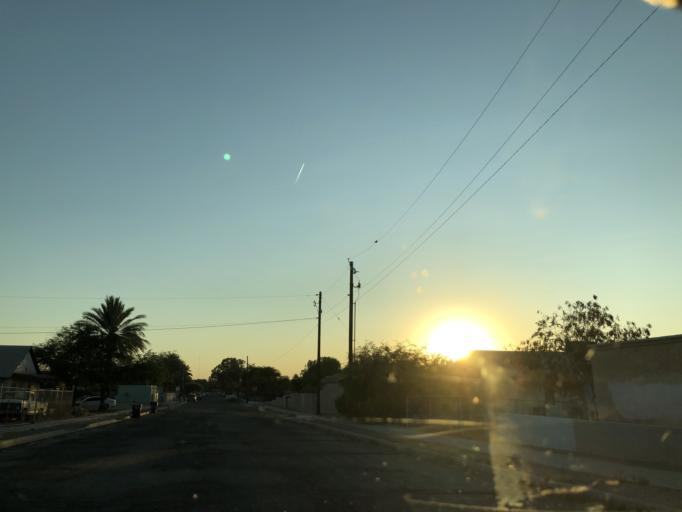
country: US
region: Arizona
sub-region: Yuma County
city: Yuma
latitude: 32.7234
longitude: -114.6272
